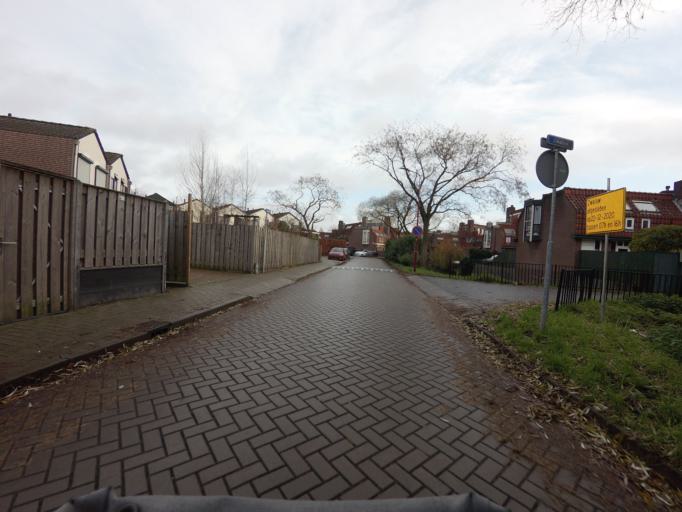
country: NL
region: Utrecht
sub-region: Gemeente Nieuwegein
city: Nieuwegein
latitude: 52.0266
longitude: 5.0706
